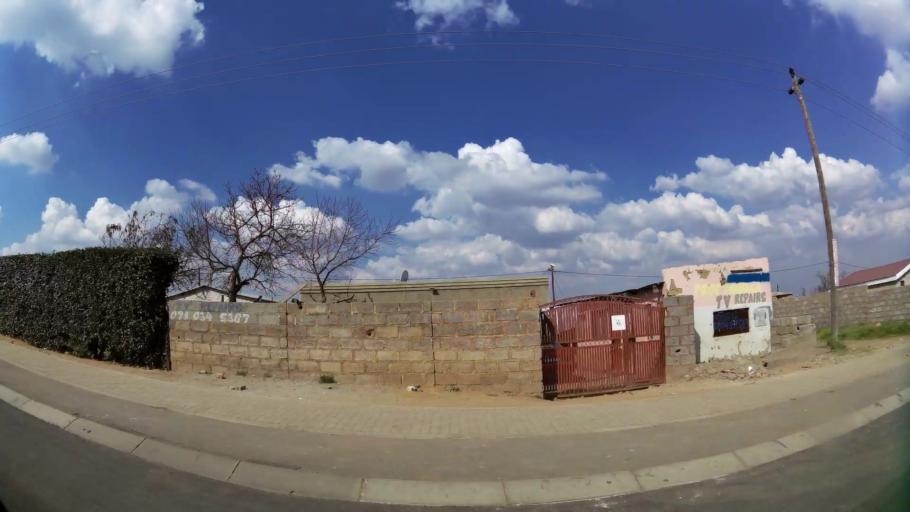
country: ZA
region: Gauteng
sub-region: City of Johannesburg Metropolitan Municipality
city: Roodepoort
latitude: -26.1926
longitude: 27.8759
